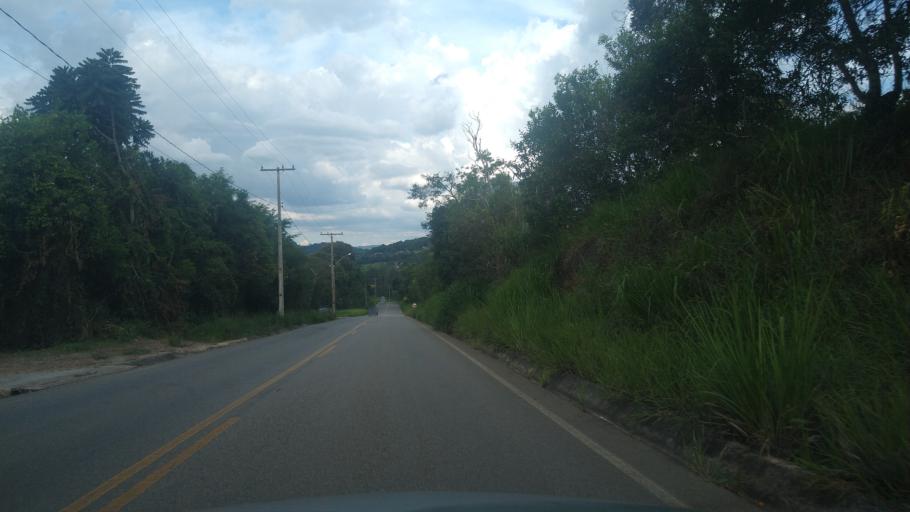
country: BR
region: Minas Gerais
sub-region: Extrema
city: Extrema
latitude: -22.8079
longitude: -46.3079
